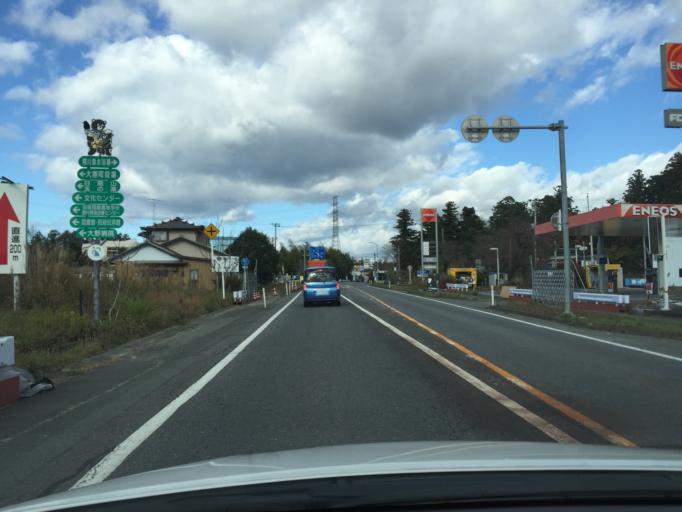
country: JP
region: Fukushima
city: Namie
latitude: 37.3950
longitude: 141.0045
